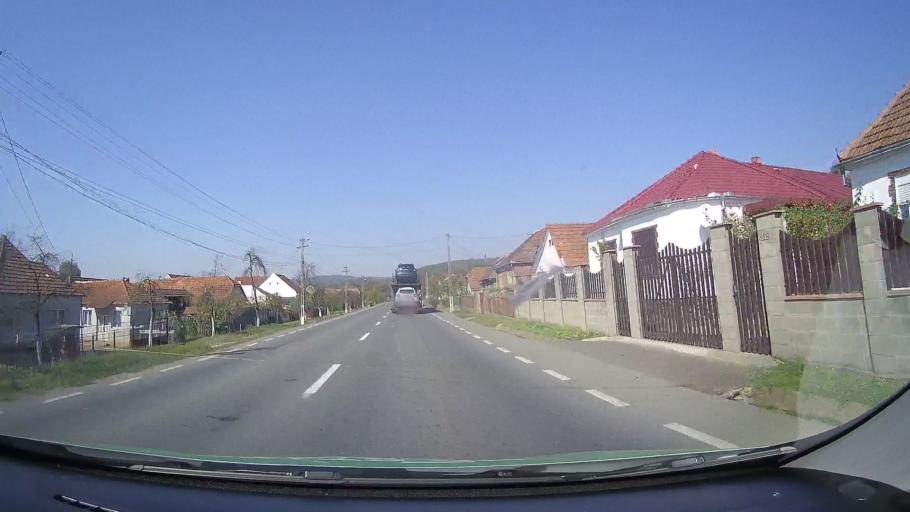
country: RO
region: Arad
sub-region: Comuna Barzava
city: Barzava
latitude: 46.0918
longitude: 22.0219
